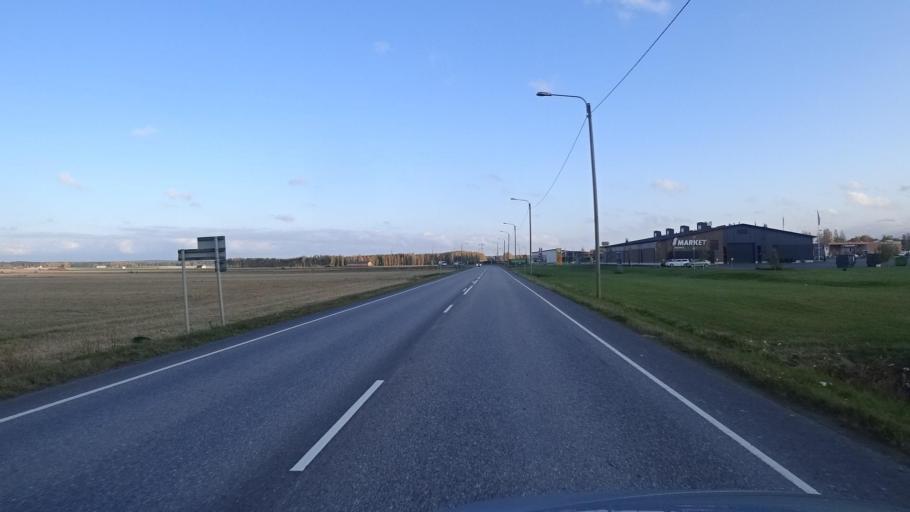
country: FI
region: Satakunta
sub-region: Rauma
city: Saekylae
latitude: 61.0478
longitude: 22.3547
